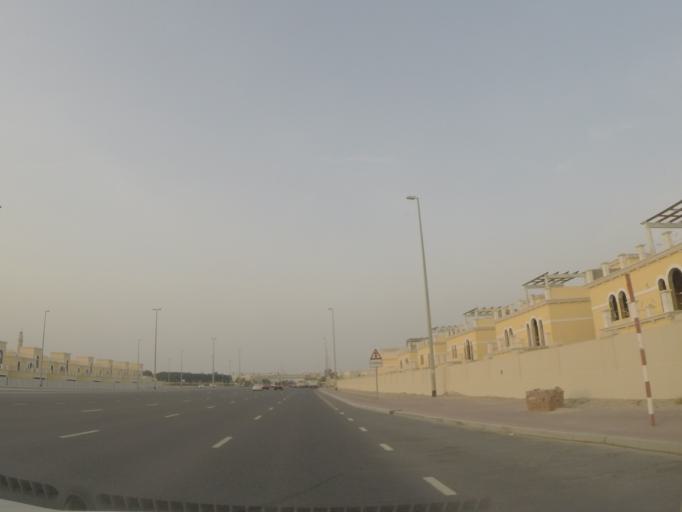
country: AE
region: Dubai
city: Dubai
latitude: 25.0508
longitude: 55.1696
